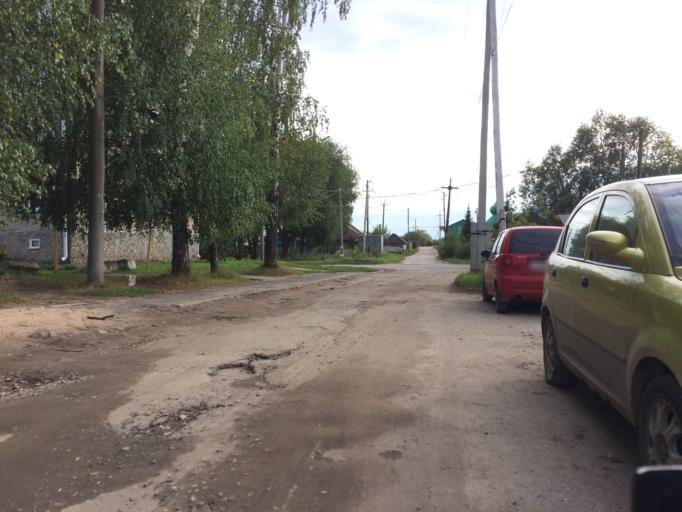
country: RU
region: Mariy-El
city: Yoshkar-Ola
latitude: 56.6574
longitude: 48.0070
